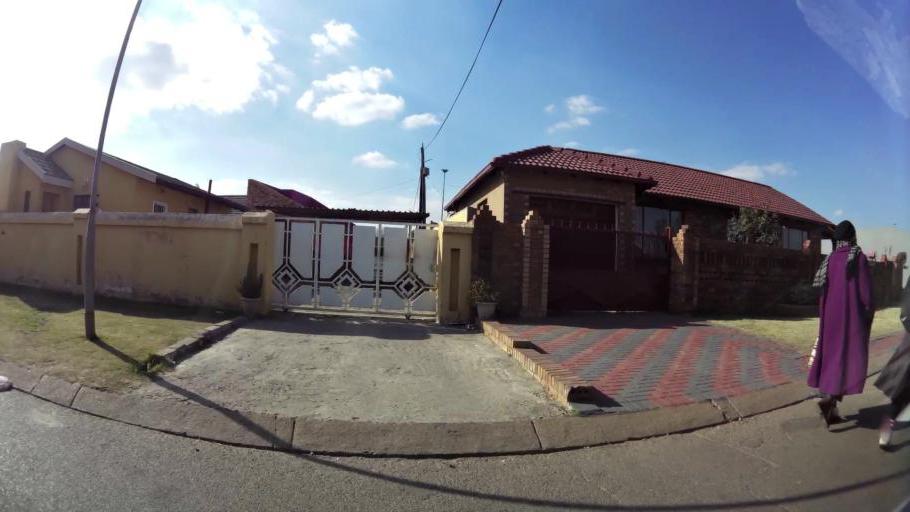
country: ZA
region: Gauteng
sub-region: City of Johannesburg Metropolitan Municipality
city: Soweto
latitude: -26.2569
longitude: 27.9050
